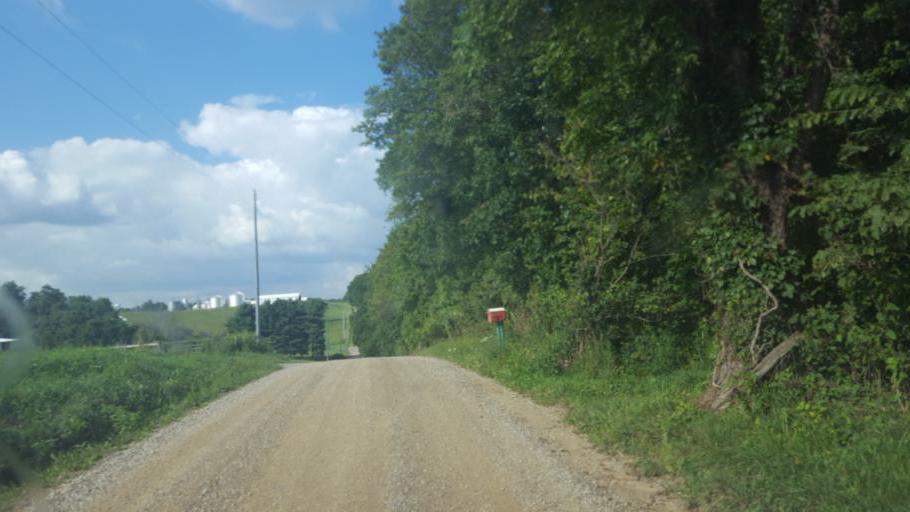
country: US
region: Ohio
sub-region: Knox County
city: Danville
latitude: 40.4491
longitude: -82.3084
